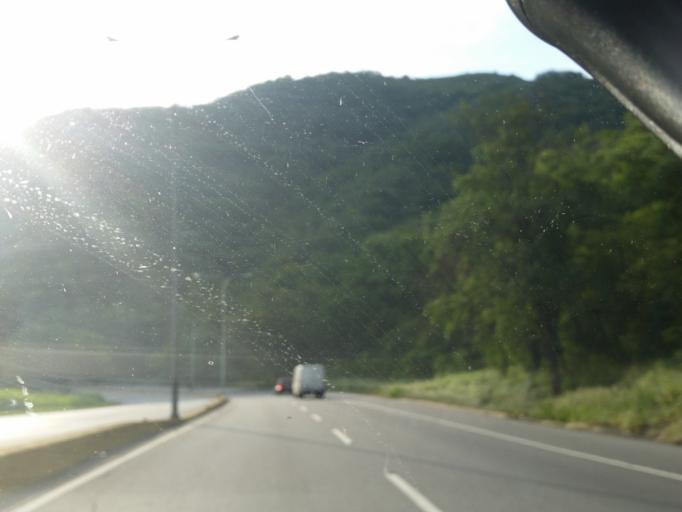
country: VE
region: Miranda
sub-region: Municipio Guaicaipuro
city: Los Teques
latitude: 10.2424
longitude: -67.0718
